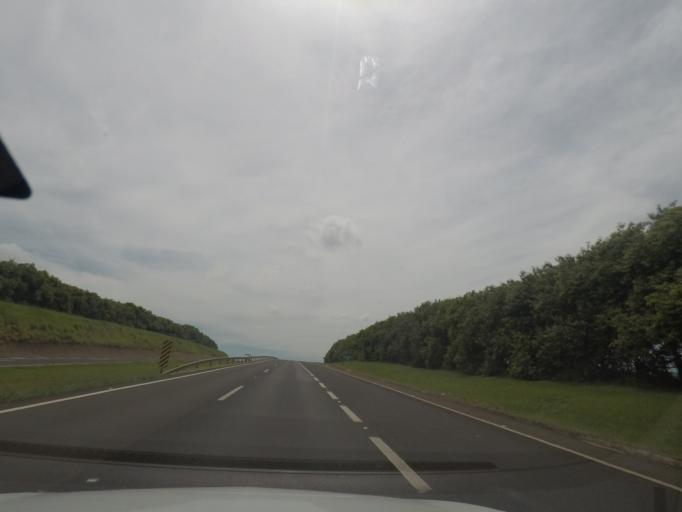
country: BR
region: Sao Paulo
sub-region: Bebedouro
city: Bebedouro
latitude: -21.0121
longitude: -48.4267
